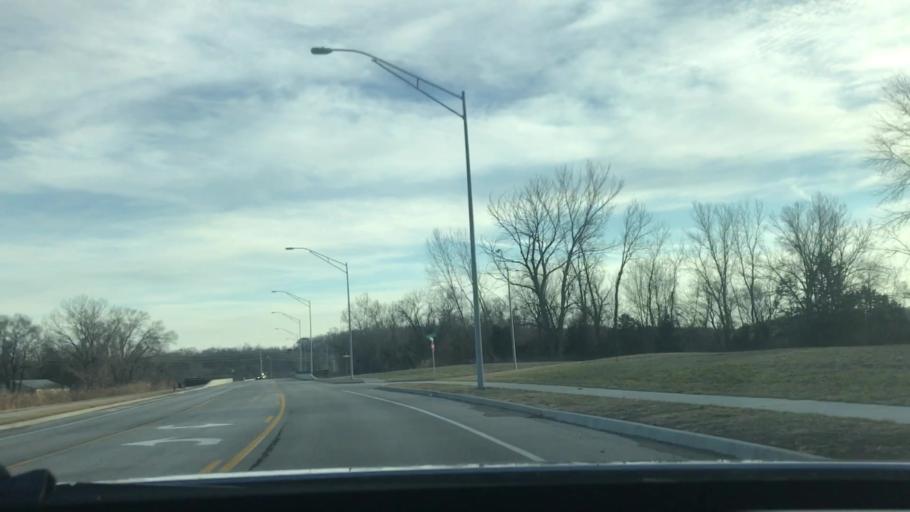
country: US
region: Missouri
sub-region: Jackson County
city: Raytown
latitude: 39.0186
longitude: -94.3882
